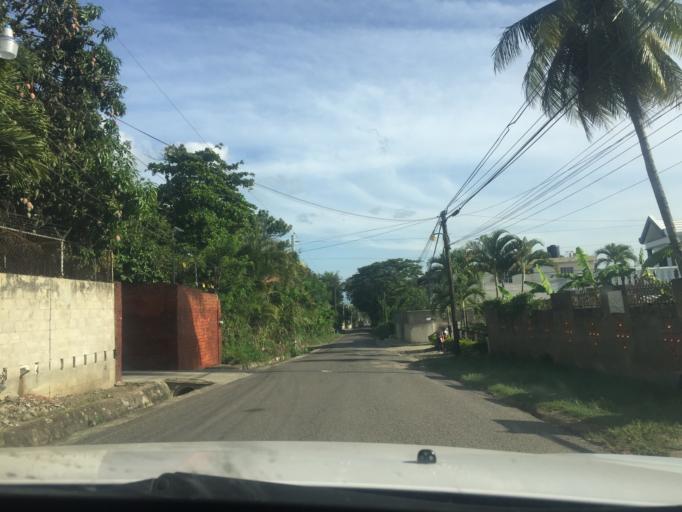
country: DO
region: Santiago
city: Tamboril
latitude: 19.4877
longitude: -70.6367
